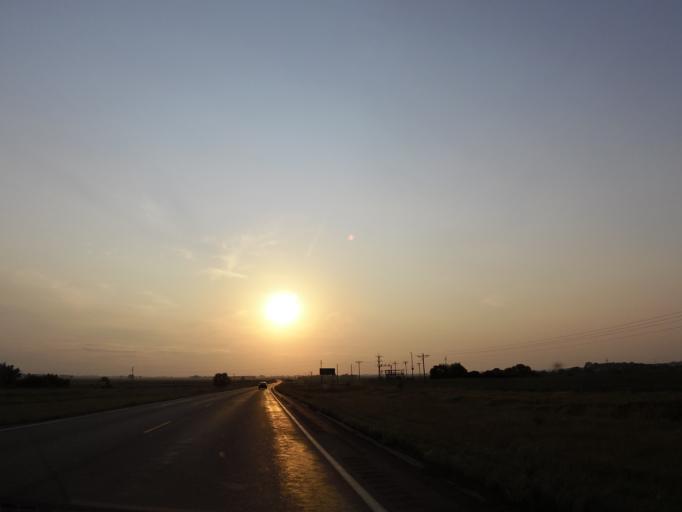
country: US
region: North Dakota
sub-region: Grand Forks County
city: Larimore
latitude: 47.7441
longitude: -97.6175
